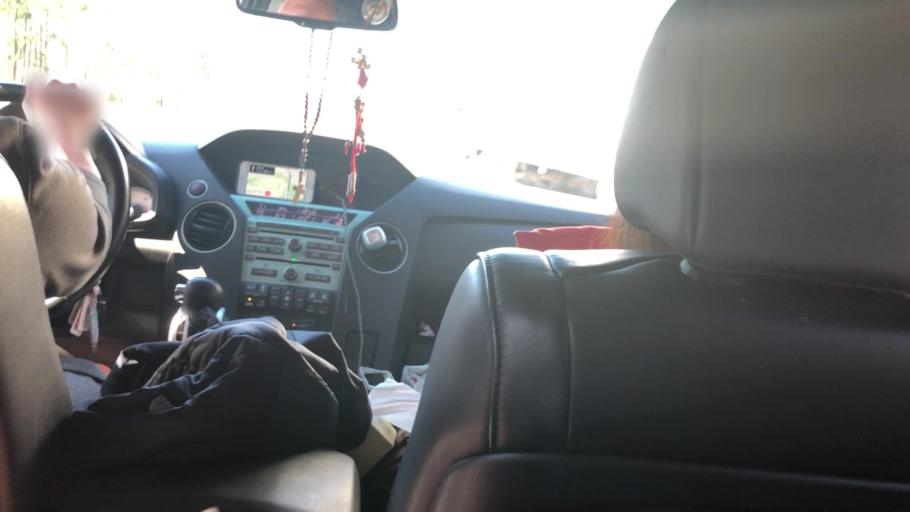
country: US
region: Louisiana
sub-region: Saint John the Baptist Parish
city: Laplace
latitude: 30.1011
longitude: -90.4836
